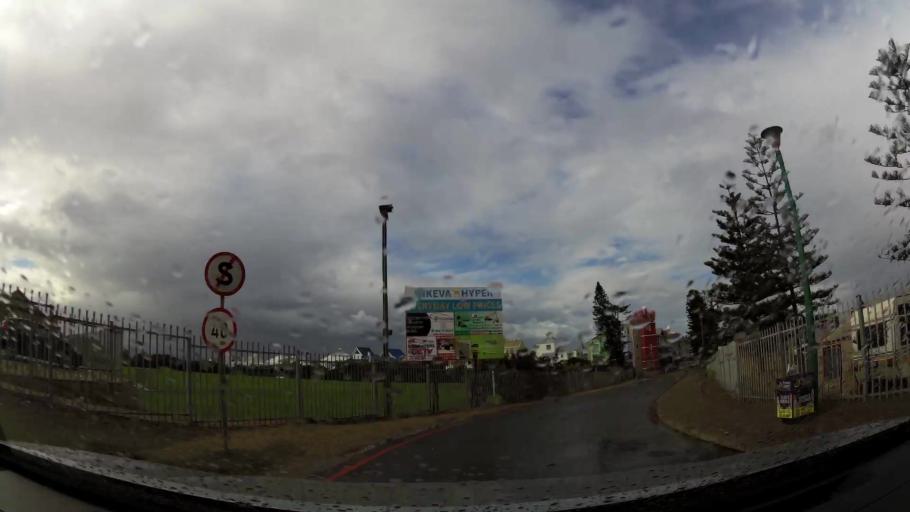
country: ZA
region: Western Cape
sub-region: Eden District Municipality
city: Mossel Bay
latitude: -34.1830
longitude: 22.1553
